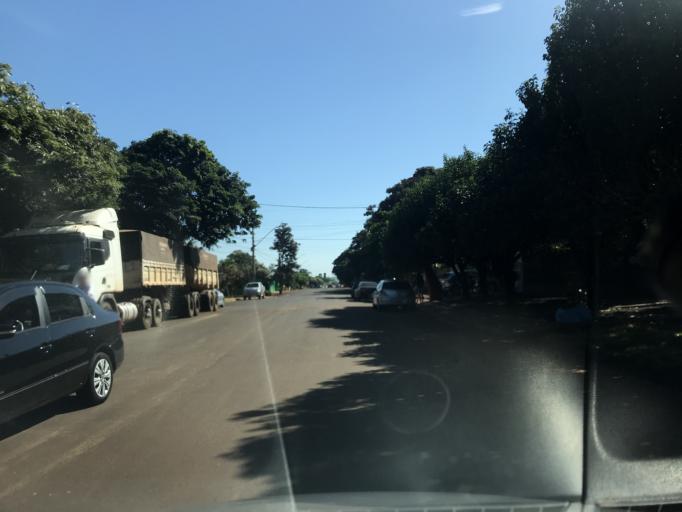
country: BR
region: Parana
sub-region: Palotina
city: Palotina
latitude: -24.2713
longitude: -53.8451
